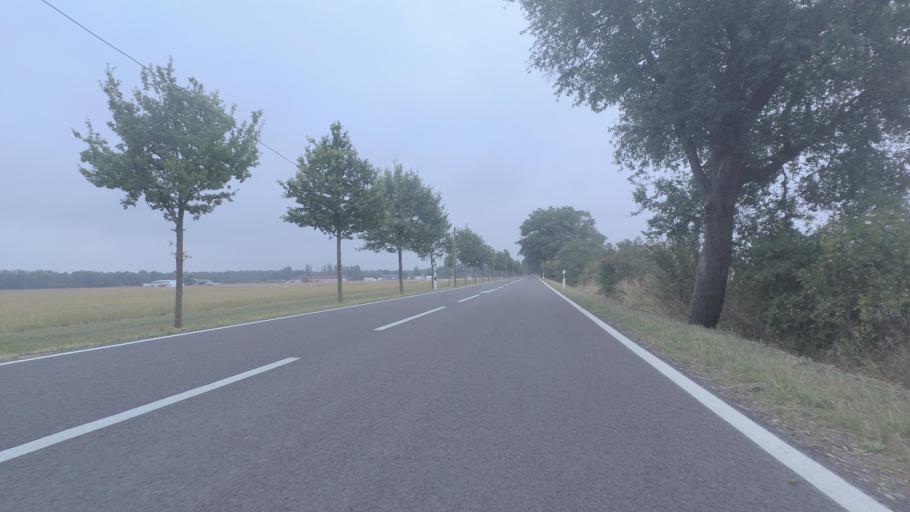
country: DE
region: Brandenburg
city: Paulinenaue
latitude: 52.6574
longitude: 12.7466
